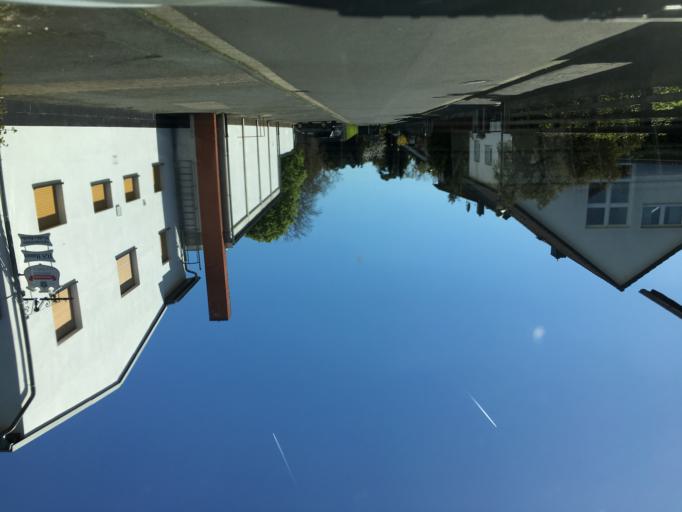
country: DE
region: Hesse
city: Obertshausen
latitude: 50.0859
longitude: 8.8618
